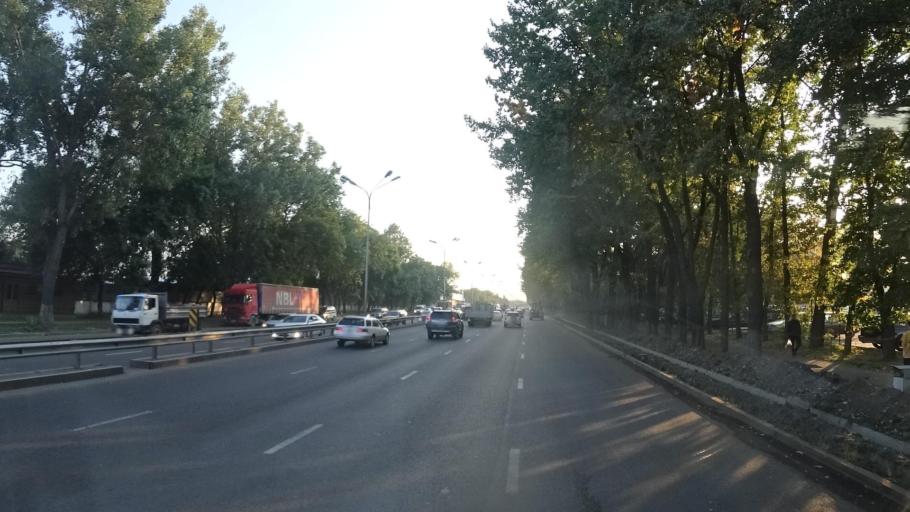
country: KZ
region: Almaty Qalasy
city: Almaty
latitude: 43.2869
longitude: 76.9224
